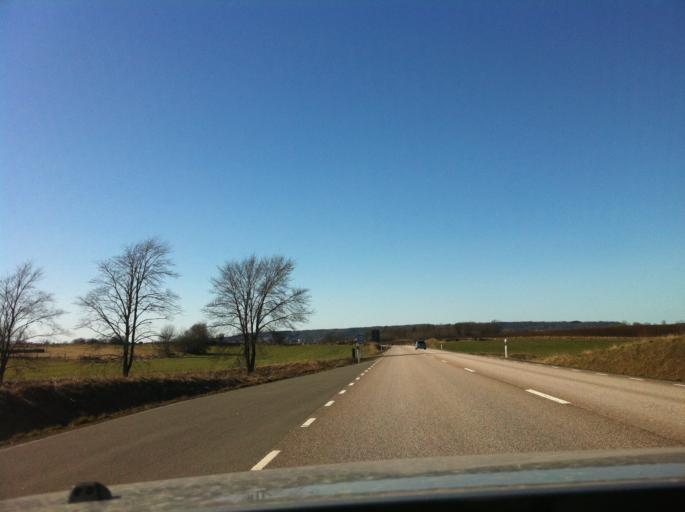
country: SE
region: Vaestra Goetaland
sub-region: Falkopings Kommun
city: Falkoeping
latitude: 58.1502
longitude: 13.6053
